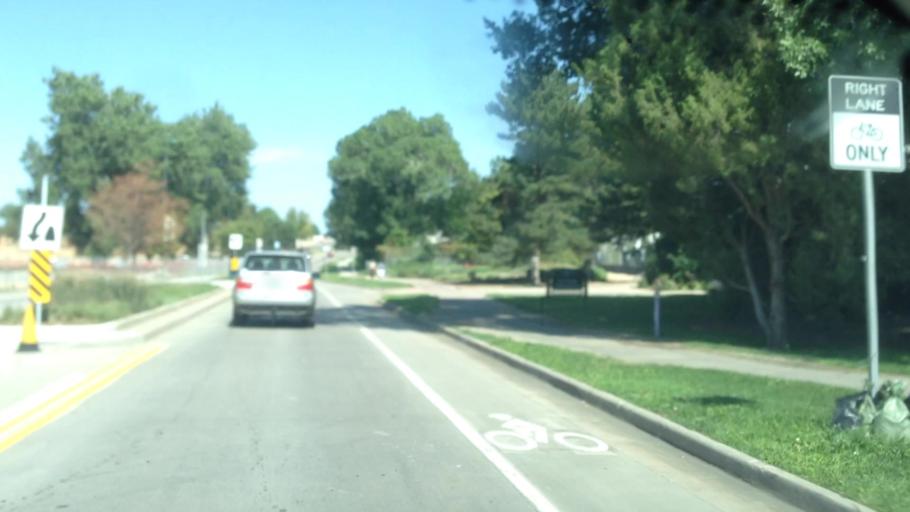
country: US
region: Colorado
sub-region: Denver County
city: Denver
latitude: 39.7508
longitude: -104.9581
